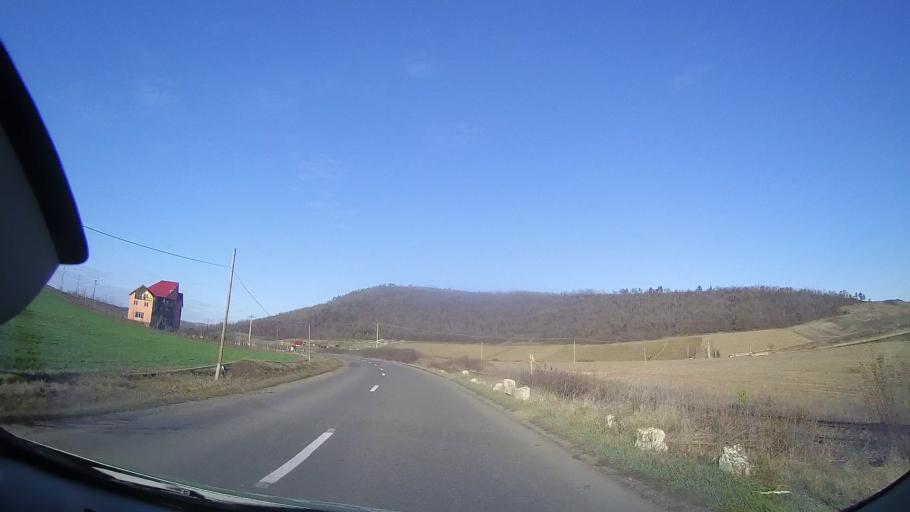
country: RO
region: Mures
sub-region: Comuna Mihesu de Campie
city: Mihesu de Campie
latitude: 46.6688
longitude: 24.1731
